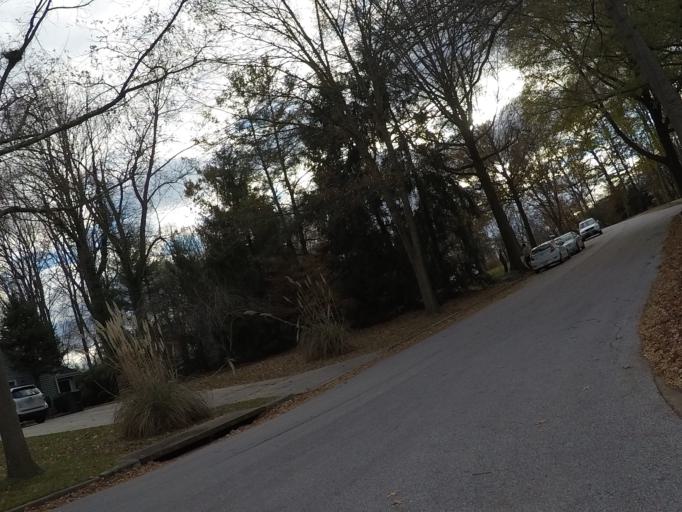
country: US
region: Maryland
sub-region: Howard County
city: Columbia
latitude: 39.2604
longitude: -76.8437
